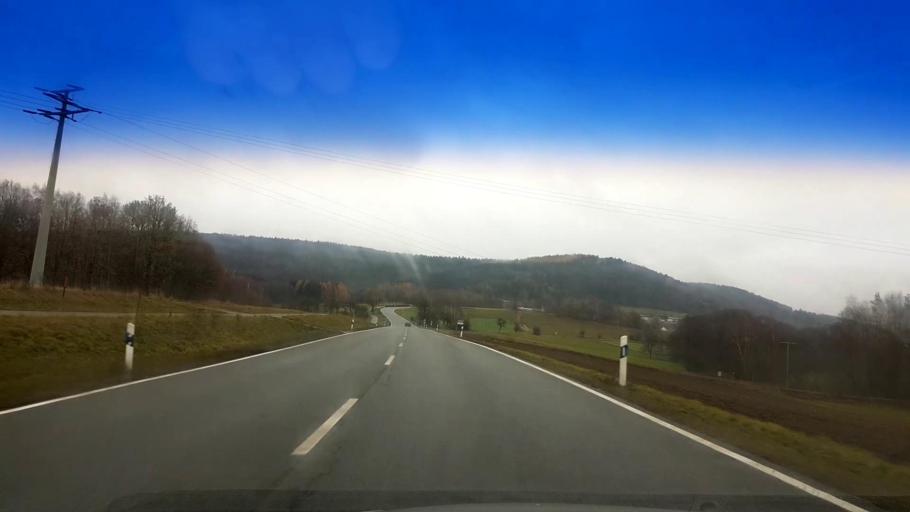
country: DE
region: Bavaria
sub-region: Upper Palatinate
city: Kemnath
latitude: 49.8646
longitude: 11.9377
